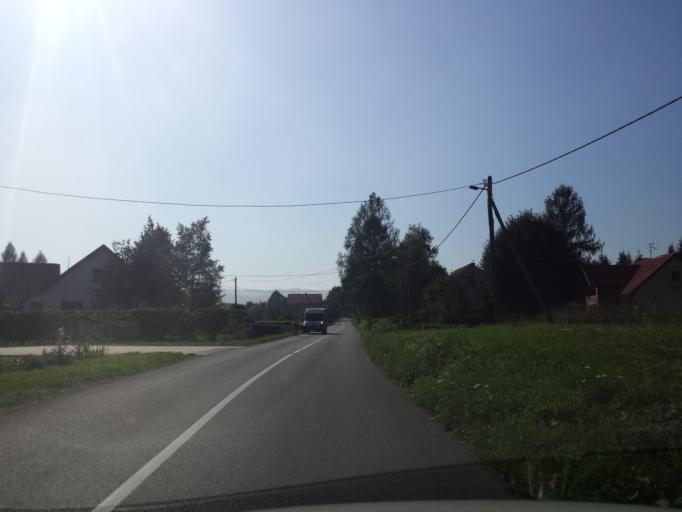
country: HR
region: Karlovacka
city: Ostarije
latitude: 45.2174
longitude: 15.3069
